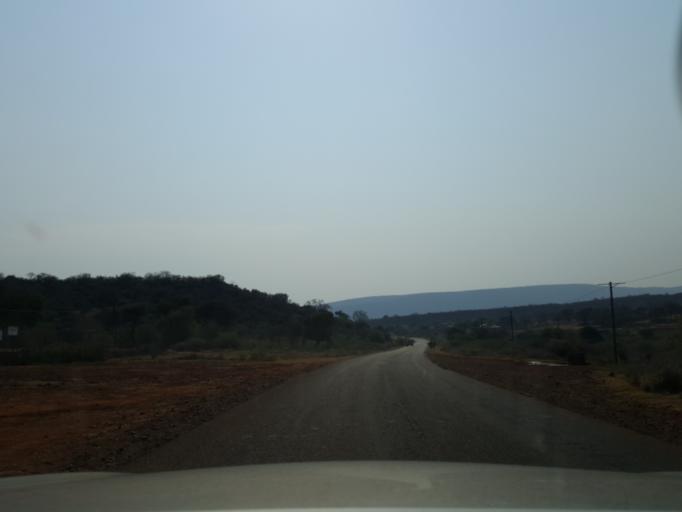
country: BW
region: South East
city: Lobatse
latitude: -25.3042
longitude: 25.8226
